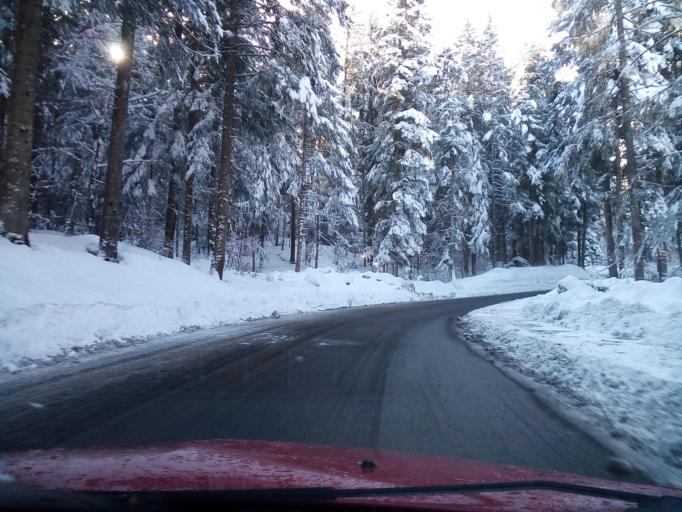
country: FR
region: Rhone-Alpes
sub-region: Departement de l'Isere
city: Le Sappey-en-Chartreuse
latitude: 45.3068
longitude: 5.7721
